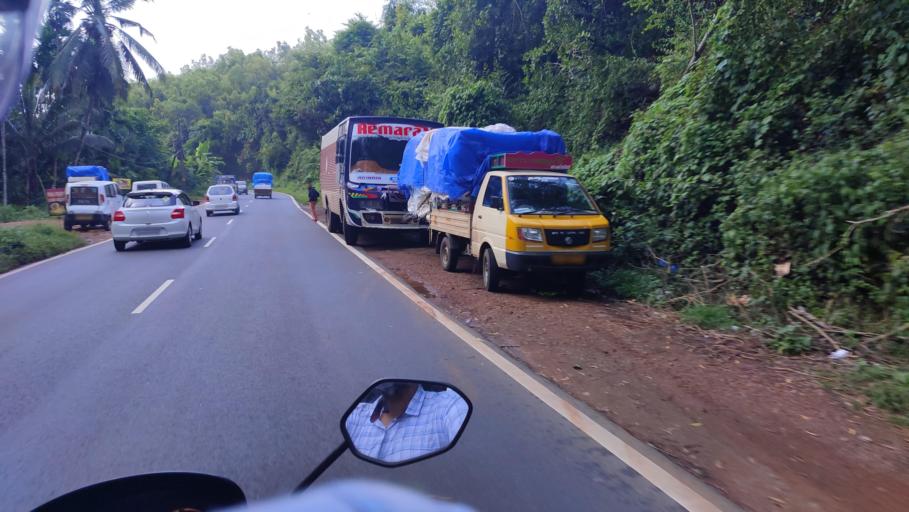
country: IN
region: Kerala
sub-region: Kasaragod District
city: Nileshwar
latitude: 12.2304
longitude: 75.1540
